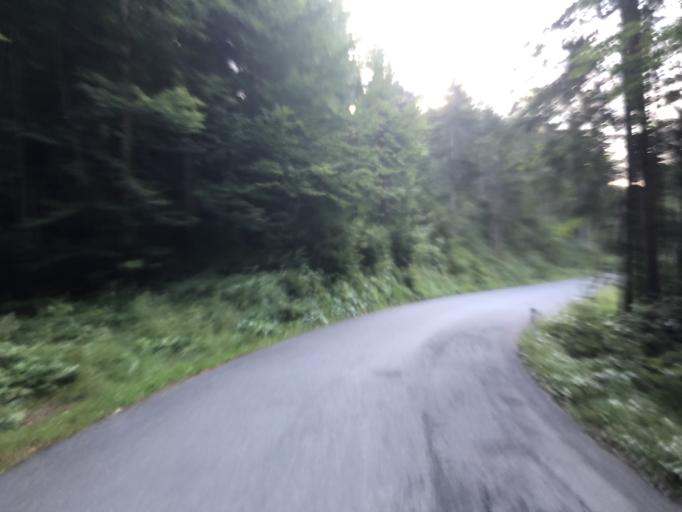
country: AT
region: Tyrol
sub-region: Politischer Bezirk Kitzbuhel
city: Schwendt
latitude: 47.5830
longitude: 12.3540
